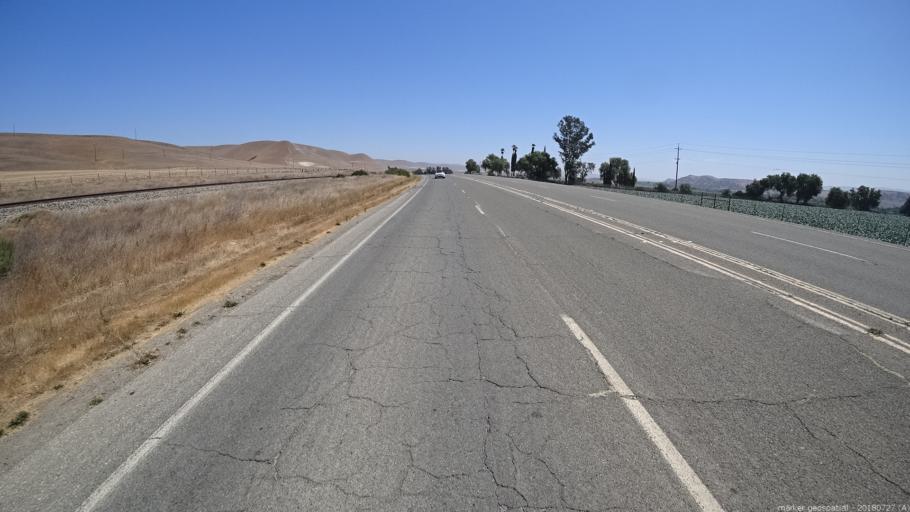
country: US
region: California
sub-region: Monterey County
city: King City
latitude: 36.1053
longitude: -120.9891
